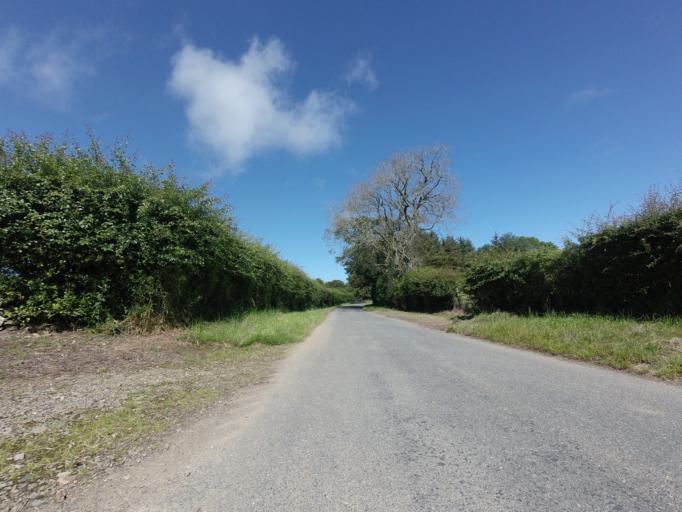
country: GB
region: Scotland
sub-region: Aberdeenshire
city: Banff
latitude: 57.6164
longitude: -2.5088
